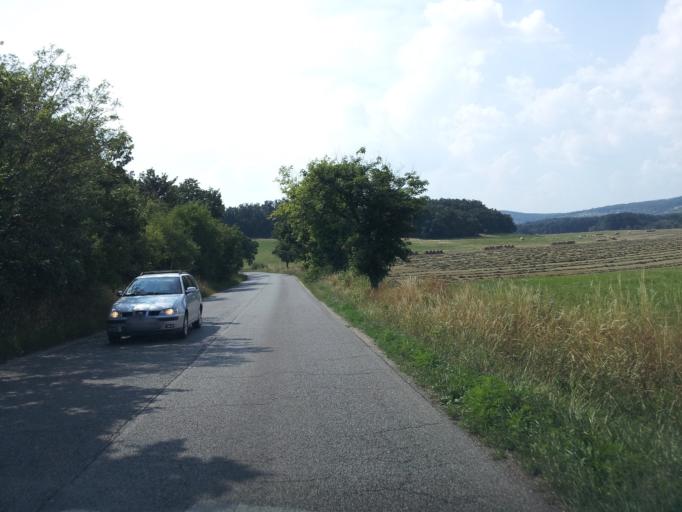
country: HU
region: Veszprem
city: Balatonfured
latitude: 46.9661
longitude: 17.8453
